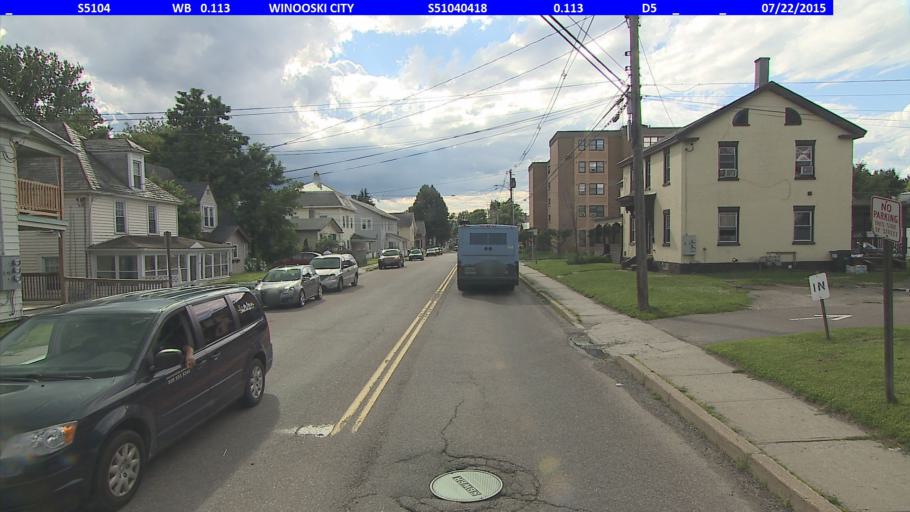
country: US
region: Vermont
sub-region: Chittenden County
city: Winooski
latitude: 44.4943
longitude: -73.1839
